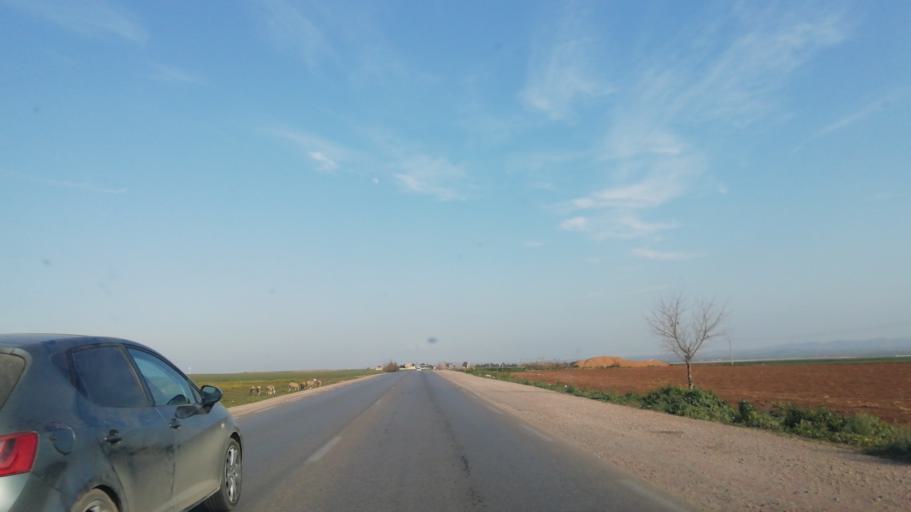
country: DZ
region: Relizane
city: Relizane
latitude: 35.8940
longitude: 0.6481
